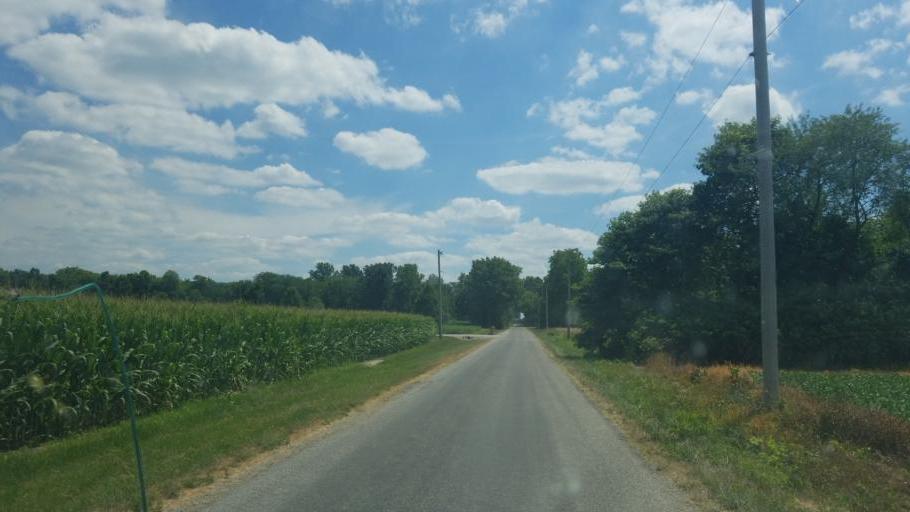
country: US
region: Ohio
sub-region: Williams County
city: Edgerton
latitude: 41.3653
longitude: -84.6902
